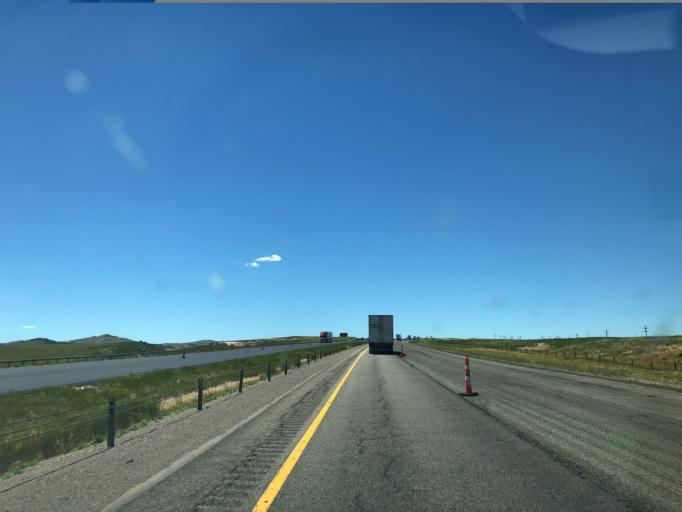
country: US
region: Wyoming
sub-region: Laramie County
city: Cheyenne
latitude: 41.0988
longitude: -105.1352
